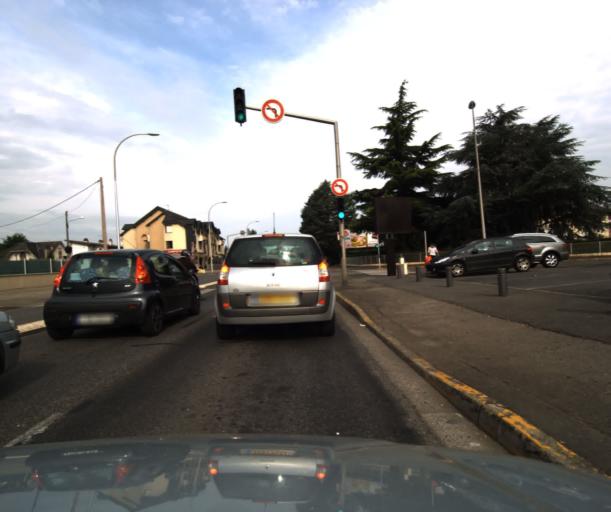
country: FR
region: Midi-Pyrenees
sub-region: Departement des Hautes-Pyrenees
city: Laloubere
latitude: 43.2204
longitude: 0.0648
